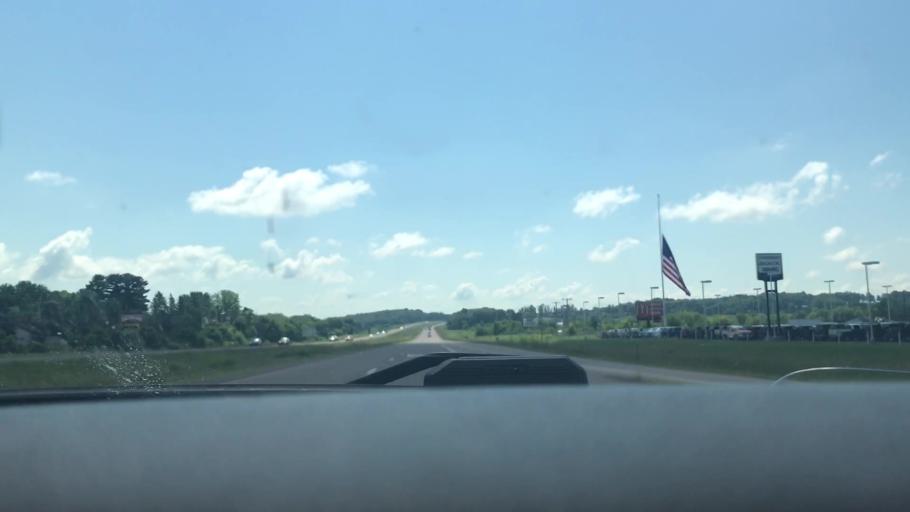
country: US
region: Wisconsin
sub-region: Chippewa County
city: Bloomer
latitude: 45.0979
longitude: -91.5019
